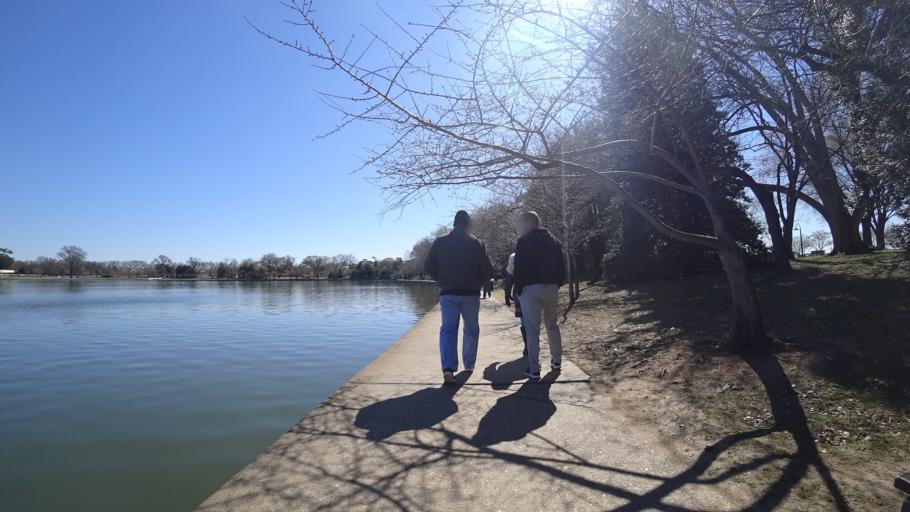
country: US
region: Washington, D.C.
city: Washington, D.C.
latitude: 38.8824
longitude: -77.0412
